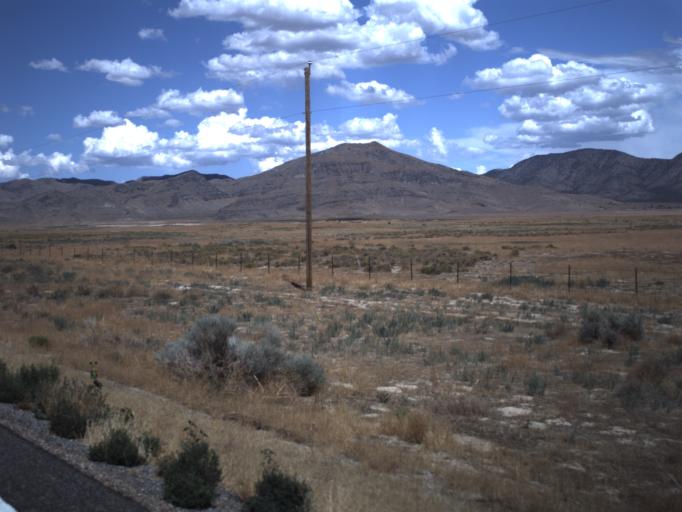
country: US
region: Utah
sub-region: Millard County
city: Delta
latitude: 39.5700
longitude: -112.3437
